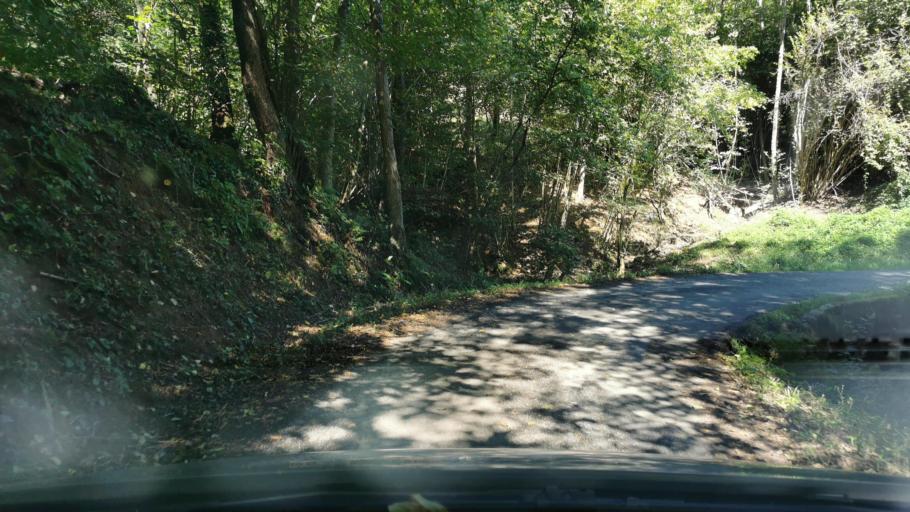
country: IT
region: Piedmont
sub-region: Provincia di Torino
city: Corio
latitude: 45.3035
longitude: 7.5192
